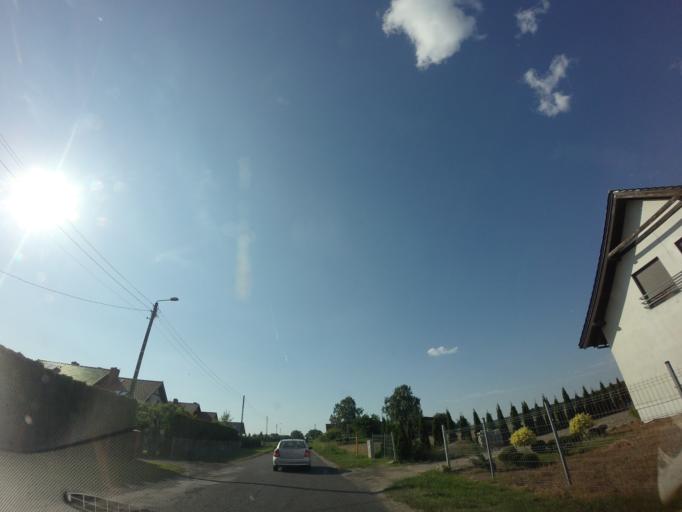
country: PL
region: West Pomeranian Voivodeship
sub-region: Powiat mysliborski
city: Barlinek
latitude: 53.0099
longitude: 15.1891
